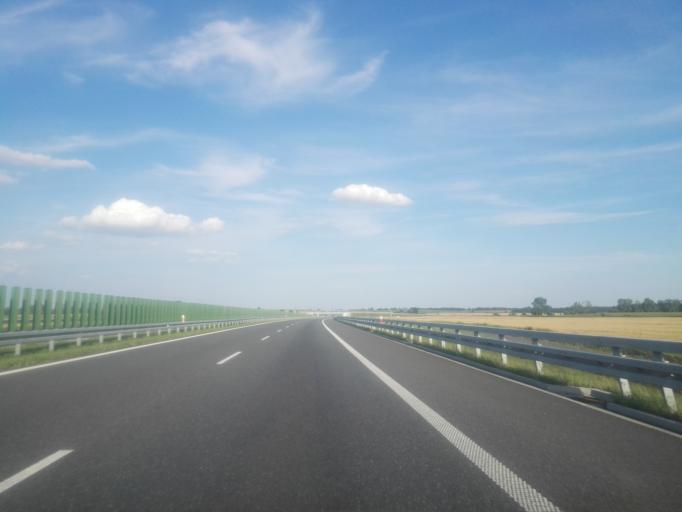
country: PL
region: Lower Silesian Voivodeship
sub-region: Powiat olesnicki
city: Sycow
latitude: 51.3052
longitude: 17.6214
